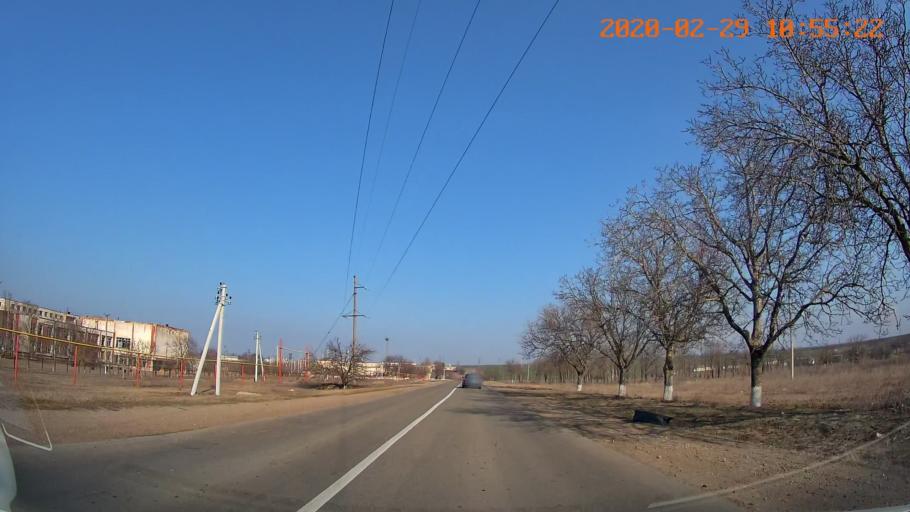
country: MD
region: Telenesti
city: Grigoriopol
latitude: 47.1331
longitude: 29.3250
